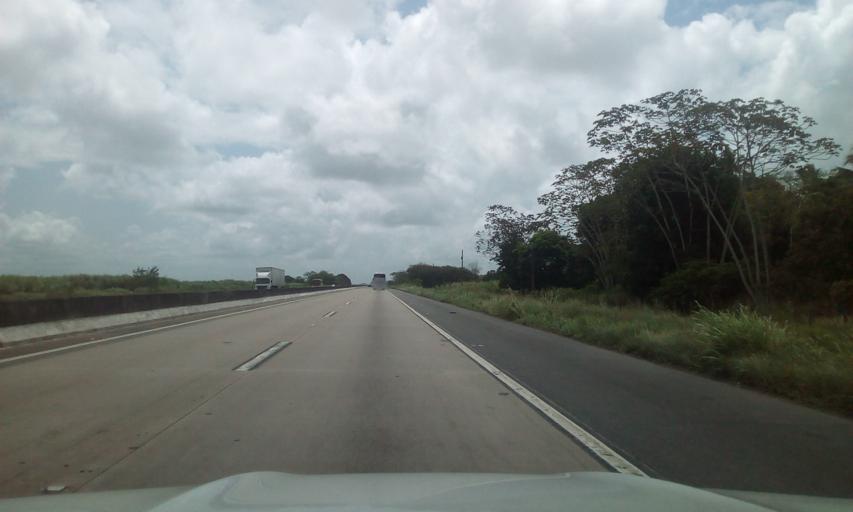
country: BR
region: Pernambuco
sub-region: Goiana
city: Goiana
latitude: -7.6460
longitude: -34.9519
